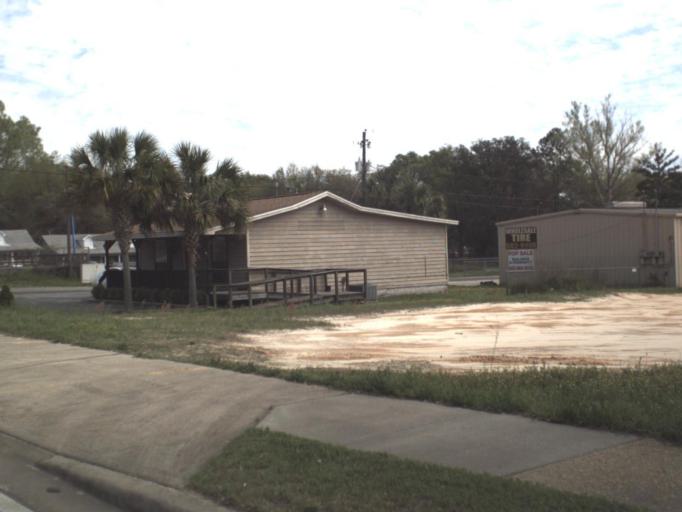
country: US
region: Florida
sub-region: Okaloosa County
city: Crestview
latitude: 30.7436
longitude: -86.5638
